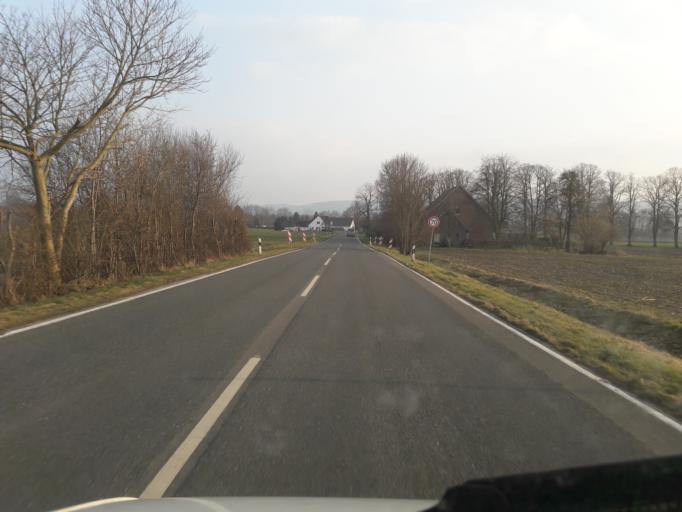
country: DE
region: North Rhine-Westphalia
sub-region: Regierungsbezirk Detmold
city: Huellhorst
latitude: 52.3339
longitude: 8.6648
